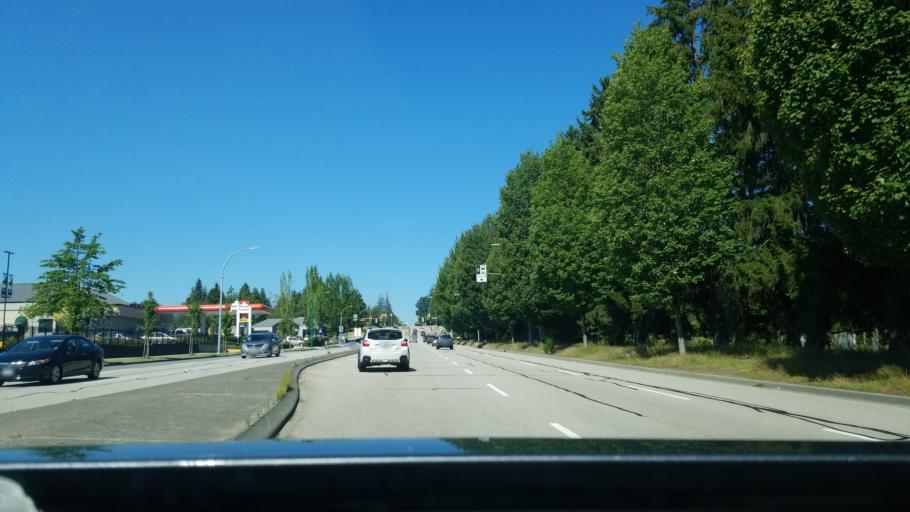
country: CA
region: British Columbia
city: Burnaby
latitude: 49.2804
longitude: -122.9667
